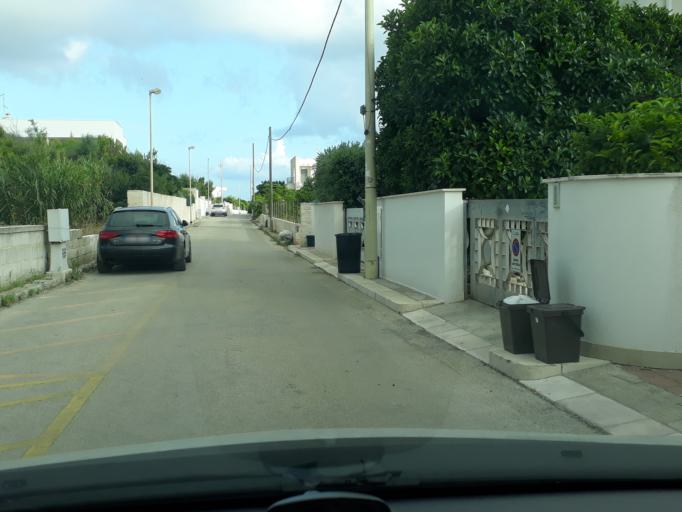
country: IT
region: Apulia
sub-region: Provincia di Brindisi
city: Carovigno
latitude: 40.7614
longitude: 17.6924
